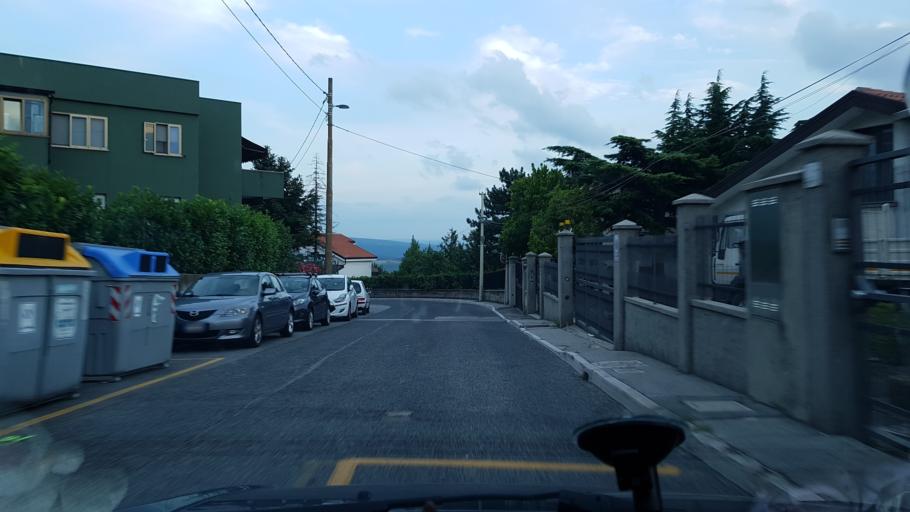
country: IT
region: Friuli Venezia Giulia
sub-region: Provincia di Trieste
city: Domio
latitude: 45.6334
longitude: 13.8229
